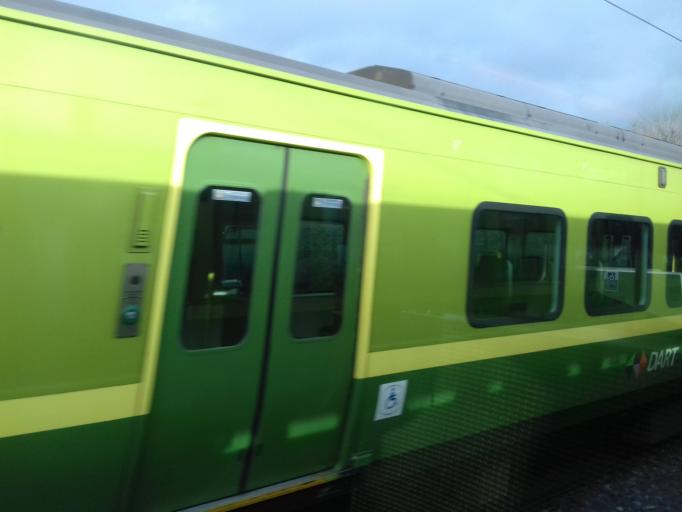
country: IE
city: Fairview
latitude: 53.3611
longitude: -6.2309
